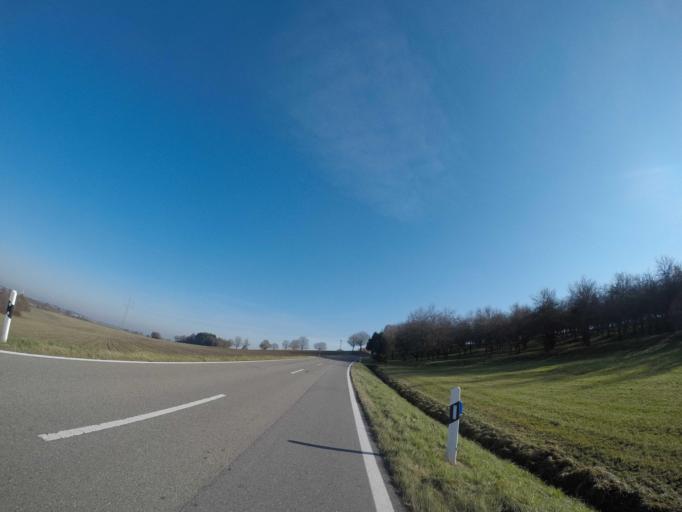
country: DE
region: Baden-Wuerttemberg
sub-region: Tuebingen Region
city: Hausen am Bussen
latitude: 48.2170
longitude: 9.6184
